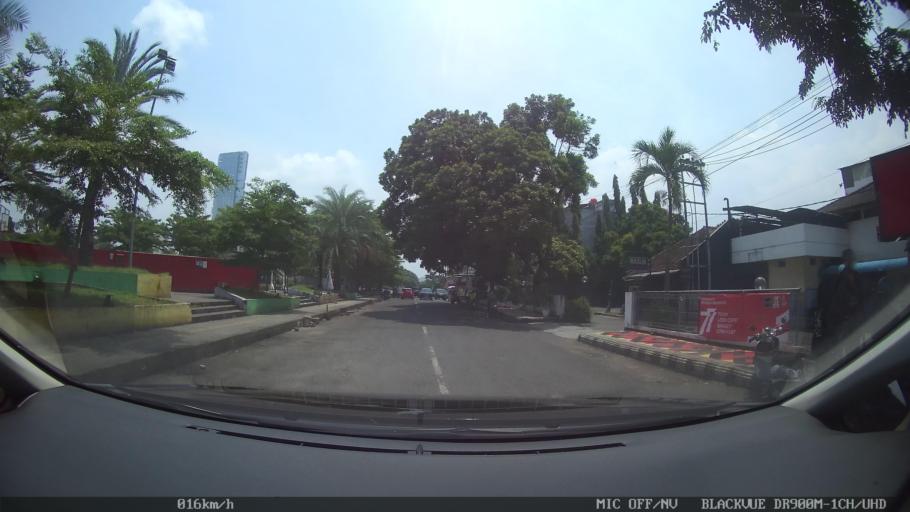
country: ID
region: Lampung
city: Bandarlampung
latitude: -5.4223
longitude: 105.2604
